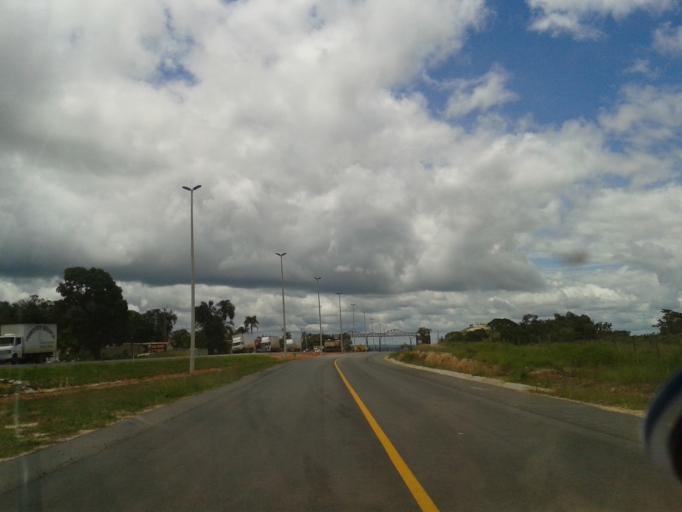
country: BR
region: Goias
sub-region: Goias
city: Goias
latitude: -15.9821
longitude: -50.0844
